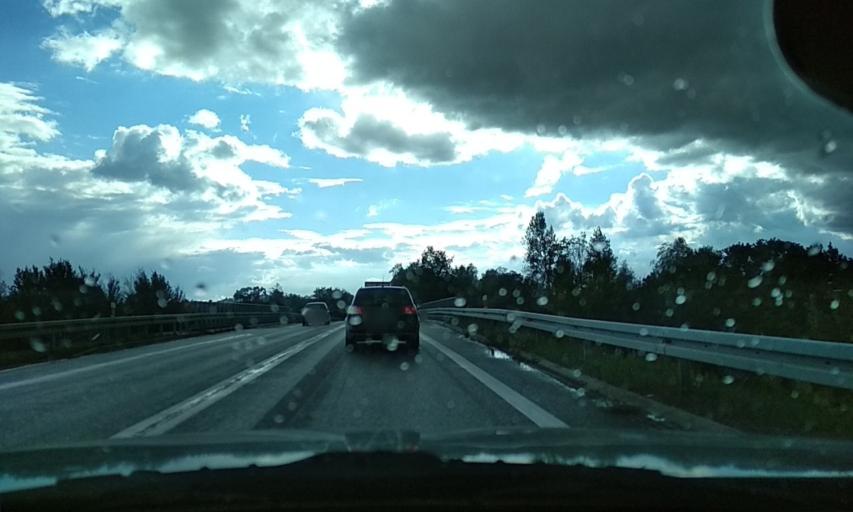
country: PL
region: Silesian Voivodeship
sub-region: Powiat gliwicki
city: Zernica
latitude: 50.2267
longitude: 18.6177
